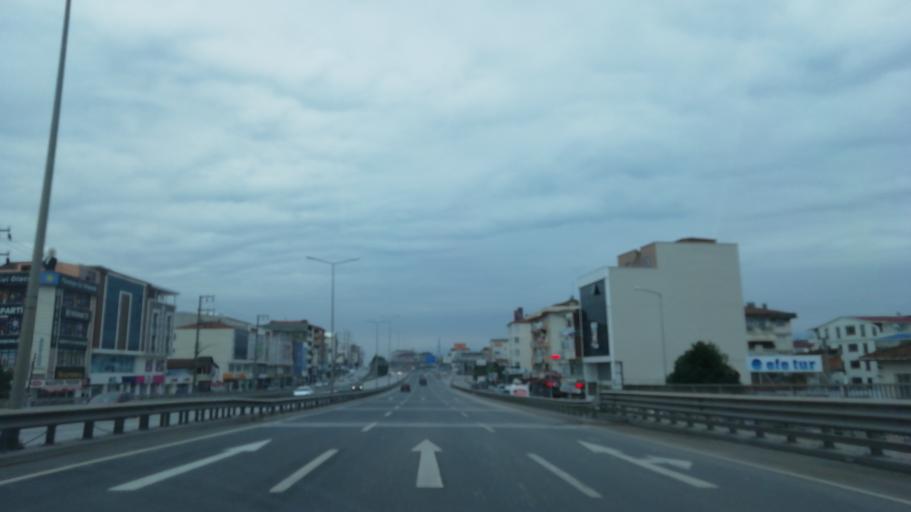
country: TR
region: Kocaeli
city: Korfez
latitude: 40.7607
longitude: 29.7878
